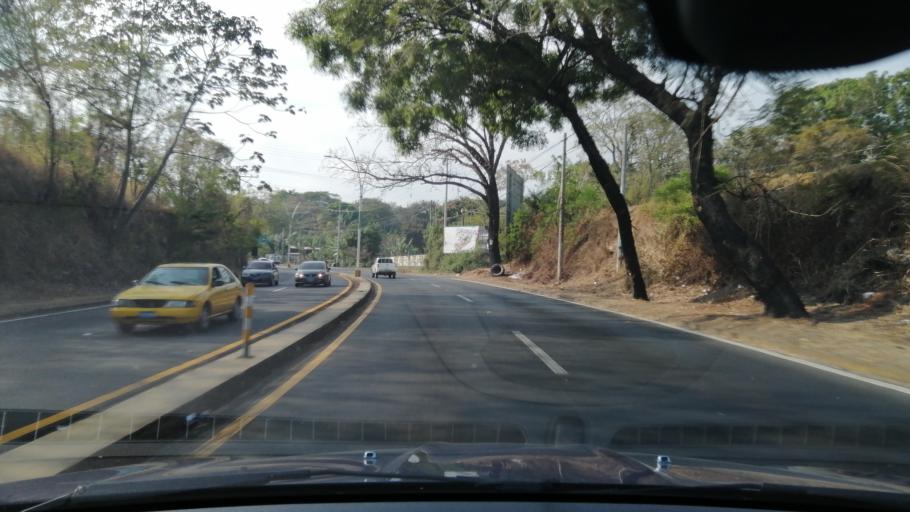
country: SV
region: Santa Ana
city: Santa Ana
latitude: 13.9598
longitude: -89.5693
